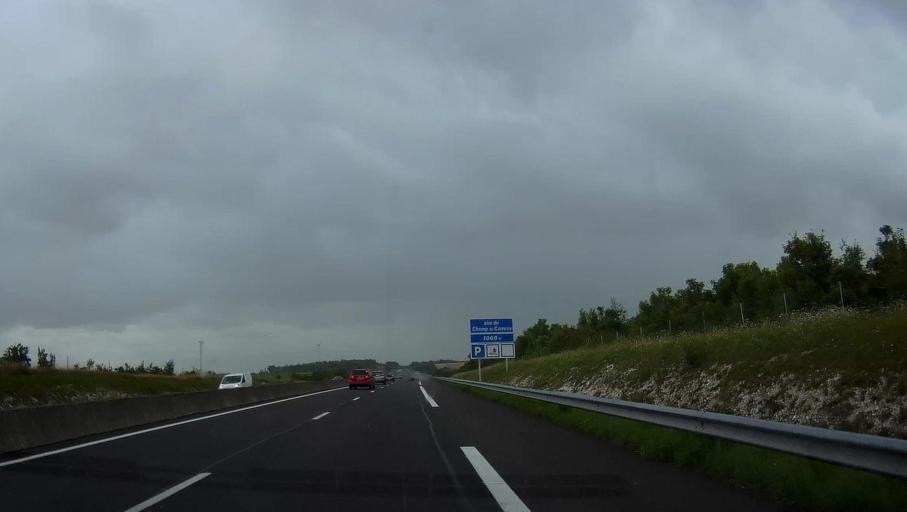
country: FR
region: Champagne-Ardenne
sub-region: Departement de l'Aube
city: Mailly-le-Camp
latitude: 48.6497
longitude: 4.1763
